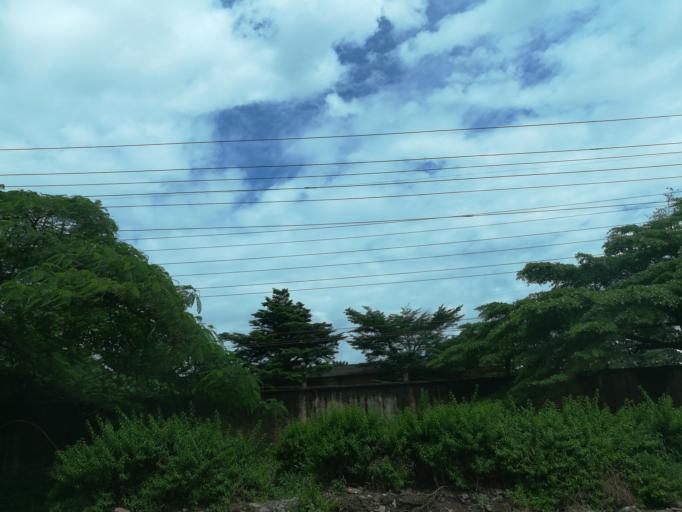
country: NG
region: Lagos
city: Ikorodu
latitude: 6.6351
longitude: 3.5119
